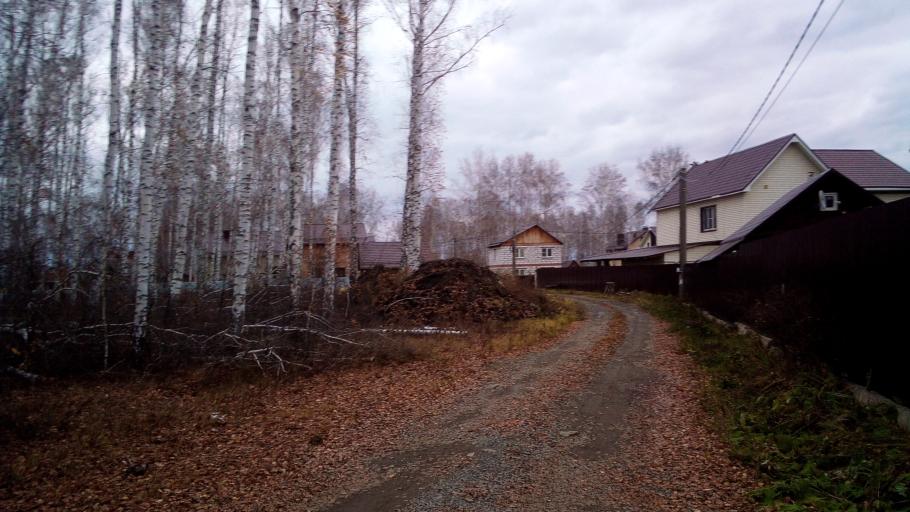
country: RU
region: Chelyabinsk
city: Sargazy
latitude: 55.1264
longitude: 61.2462
